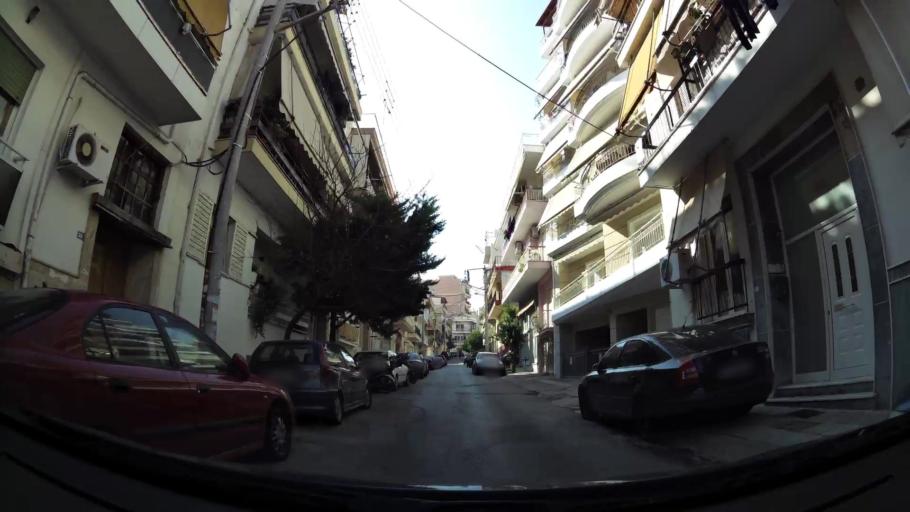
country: GR
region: Attica
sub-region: Nomos Piraios
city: Keratsini
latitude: 37.9647
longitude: 23.6315
